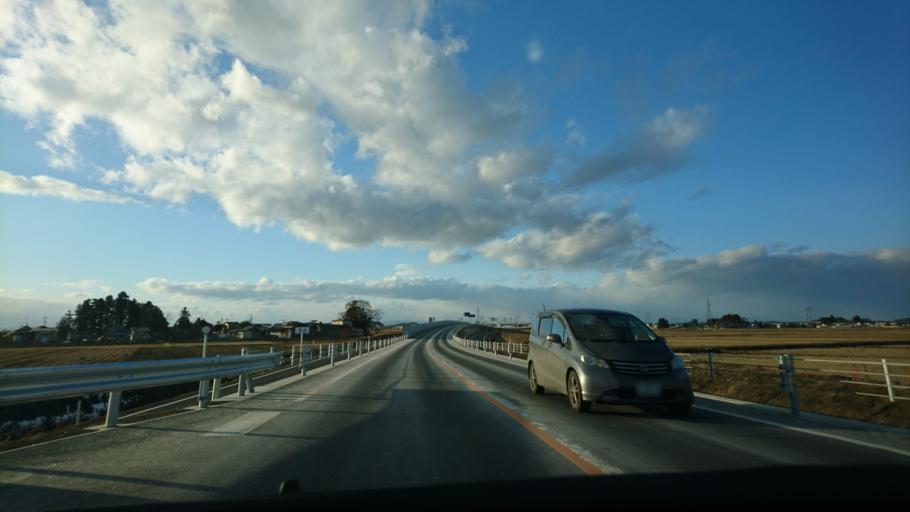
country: JP
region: Miyagi
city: Wakuya
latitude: 38.6879
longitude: 141.2241
